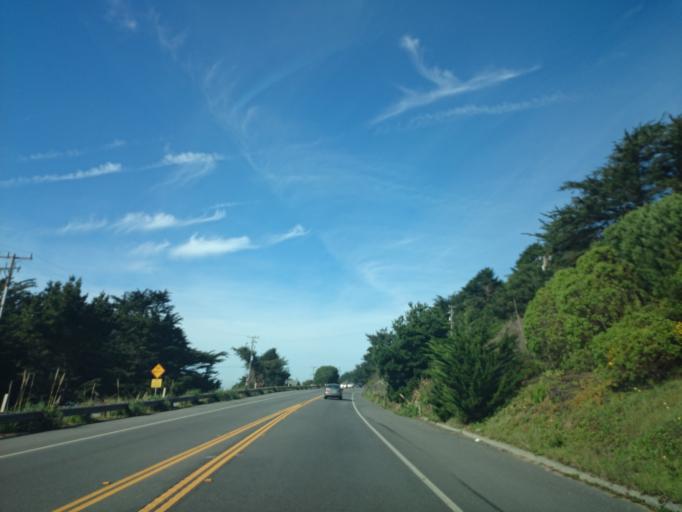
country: US
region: California
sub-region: San Mateo County
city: Moss Beach
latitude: 37.5296
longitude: -122.5154
